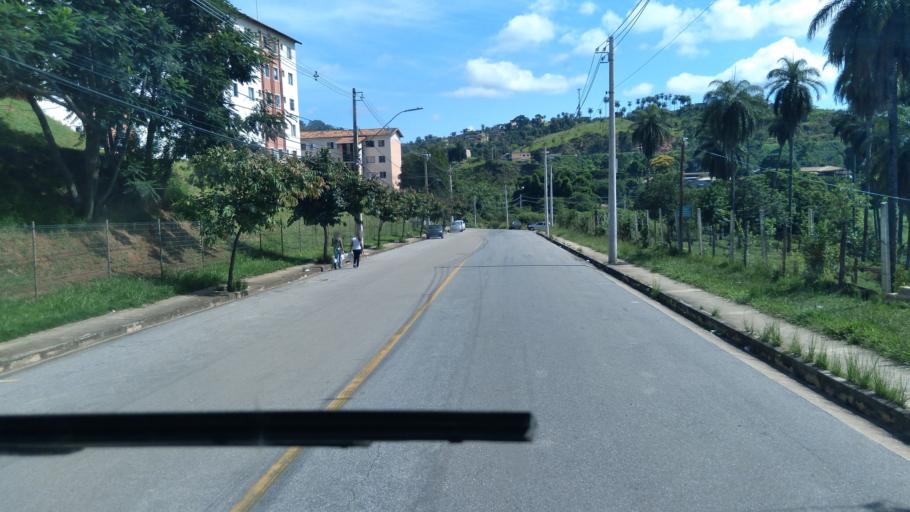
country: BR
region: Minas Gerais
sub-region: Santa Luzia
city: Santa Luzia
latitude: -19.8430
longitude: -43.8784
